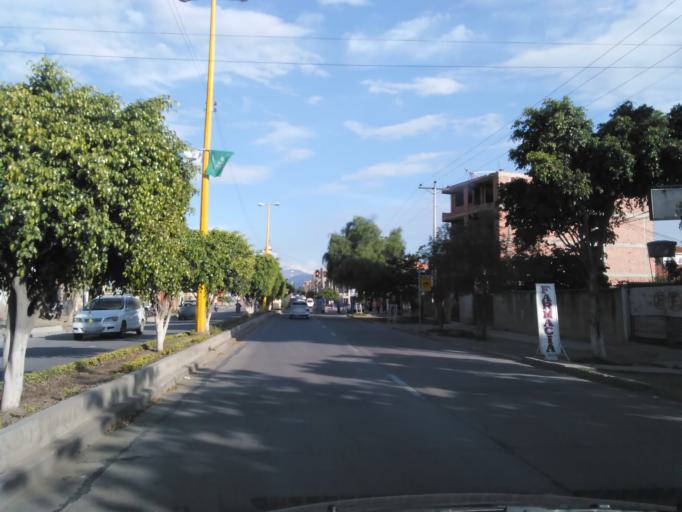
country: BO
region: Cochabamba
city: Cochabamba
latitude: -17.3522
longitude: -66.1906
